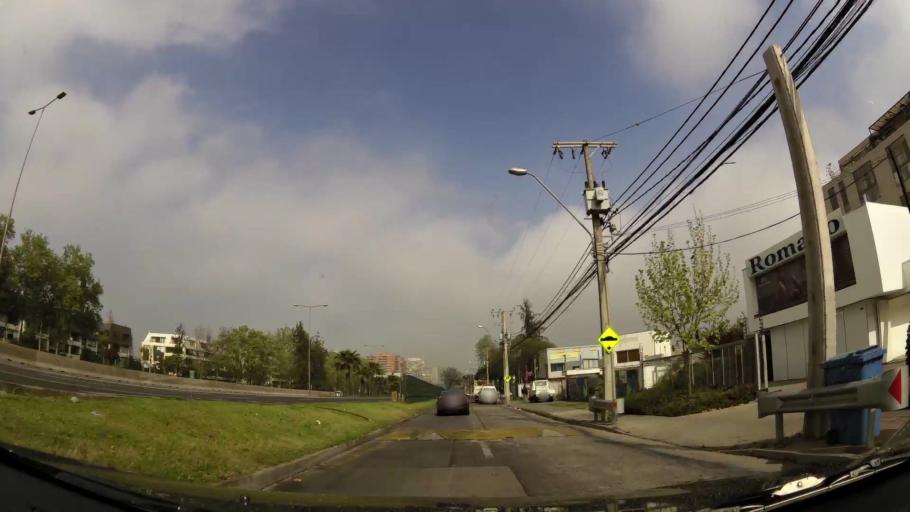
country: CL
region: Santiago Metropolitan
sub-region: Provincia de Santiago
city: Villa Presidente Frei, Nunoa, Santiago, Chile
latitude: -33.3903
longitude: -70.5503
